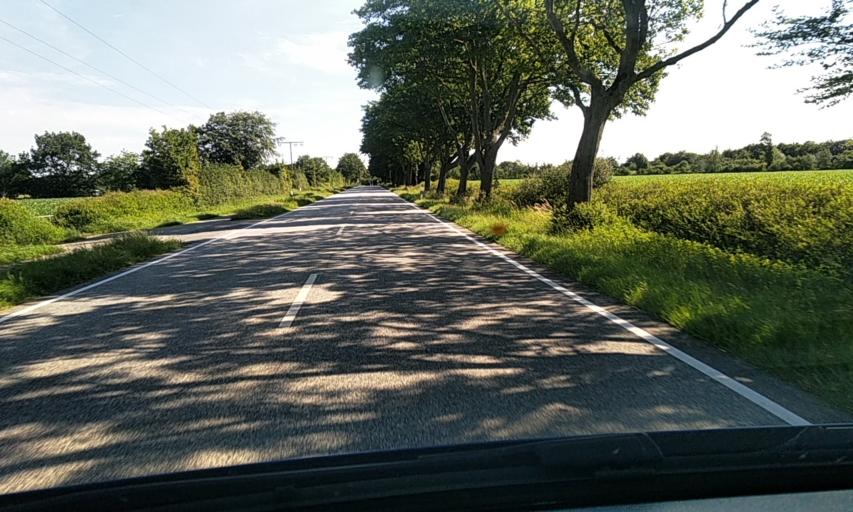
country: DE
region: Schleswig-Holstein
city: Fockbek
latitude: 54.2941
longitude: 9.5859
